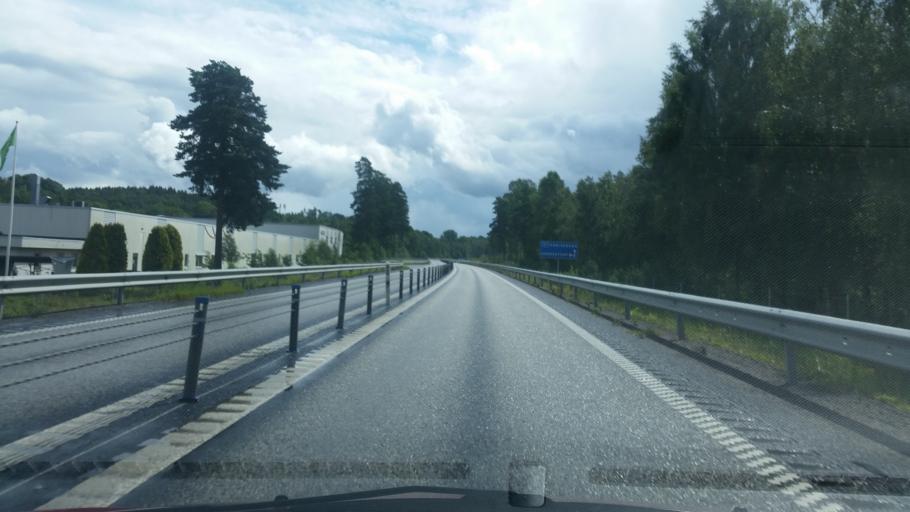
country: SE
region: Joenkoeping
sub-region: Gislaveds Kommun
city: Gislaved
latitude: 57.2717
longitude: 13.6204
